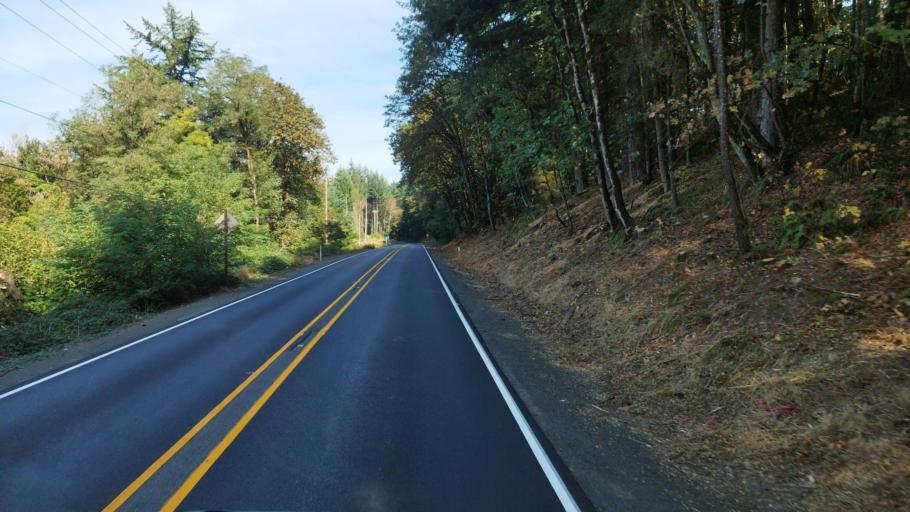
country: US
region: Oregon
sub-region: Washington County
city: Bethany
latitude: 45.5985
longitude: -122.8658
